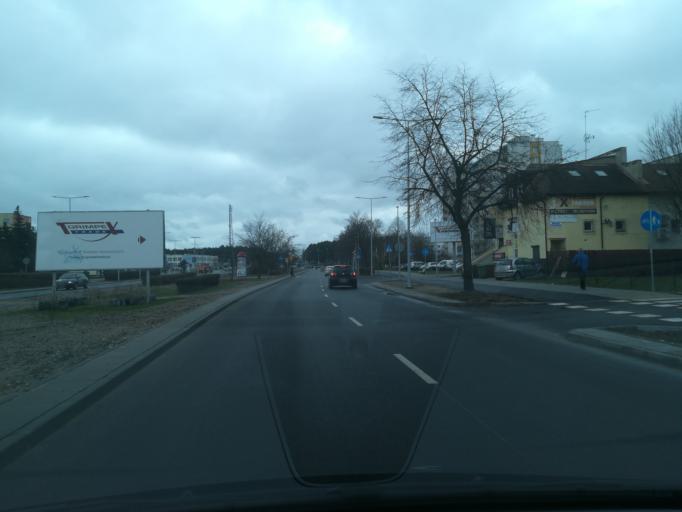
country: PL
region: Kujawsko-Pomorskie
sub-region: Powiat torunski
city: Lubicz Dolny
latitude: 53.0247
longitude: 18.6880
